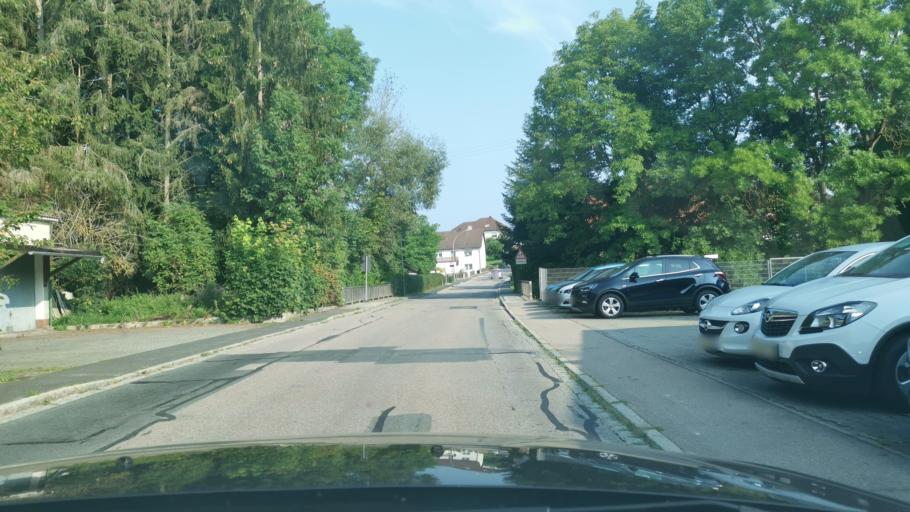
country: DE
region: Bavaria
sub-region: Upper Palatinate
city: Schnaittenbach
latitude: 49.5494
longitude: 12.0061
